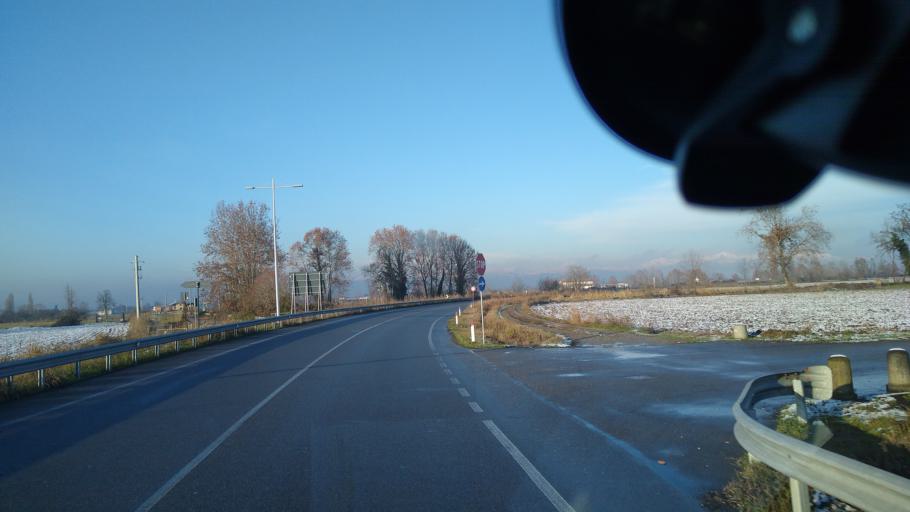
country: IT
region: Lombardy
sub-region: Provincia di Bergamo
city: Misano di Gera d'Adda
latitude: 45.4778
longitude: 9.6153
